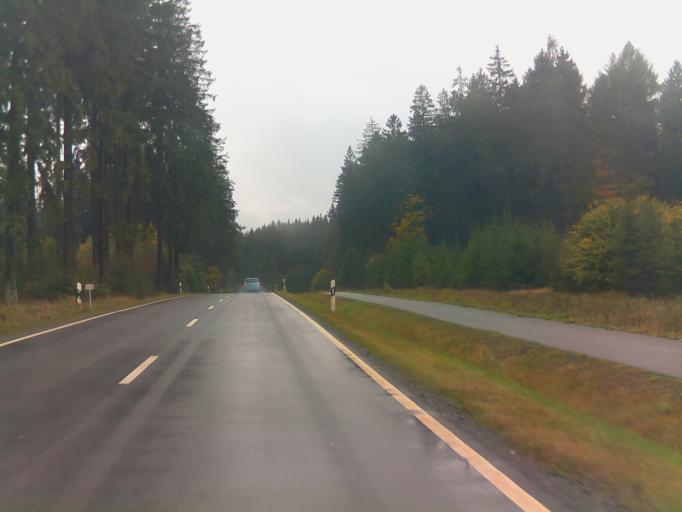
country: DE
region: Bavaria
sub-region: Upper Franconia
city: Tschirn
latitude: 50.3804
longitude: 11.4310
